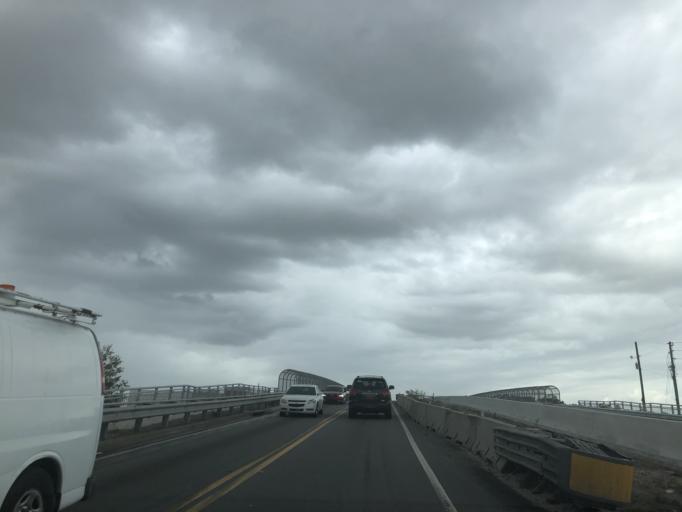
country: US
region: Florida
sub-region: Orange County
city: Taft
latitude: 28.4214
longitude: -81.3924
